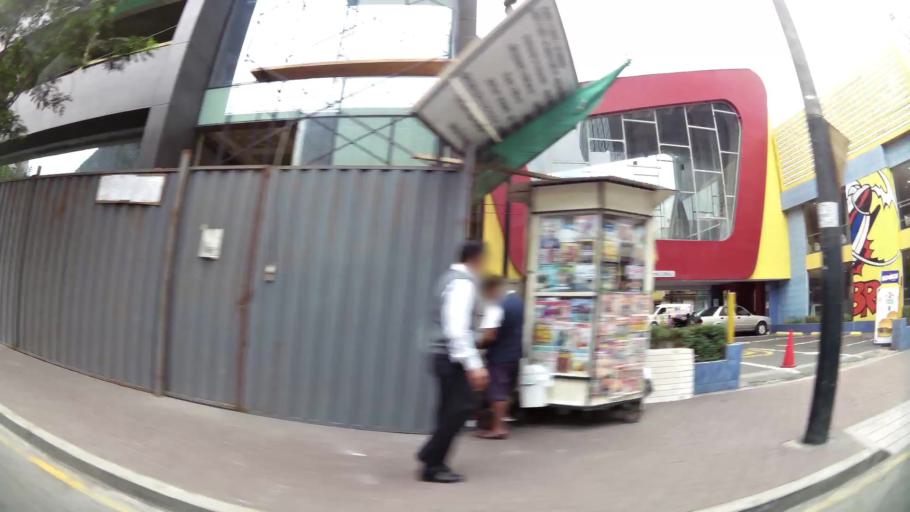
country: PE
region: Lima
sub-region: Lima
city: San Isidro
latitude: -12.0970
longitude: -77.0360
